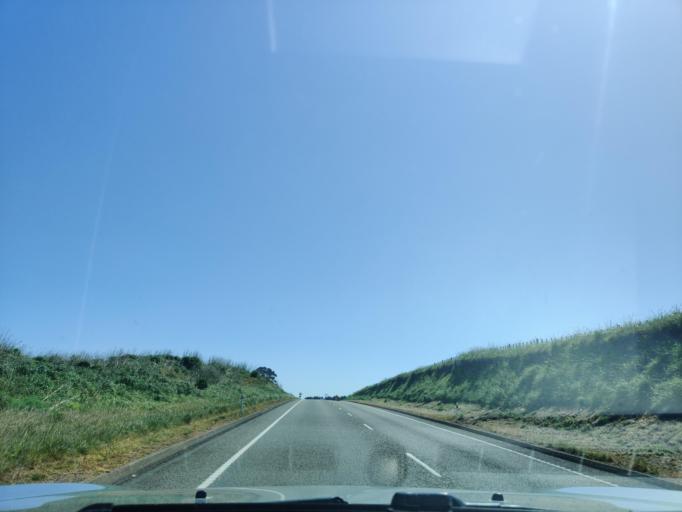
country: NZ
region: Taranaki
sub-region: South Taranaki District
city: Patea
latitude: -39.7527
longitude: 174.5381
